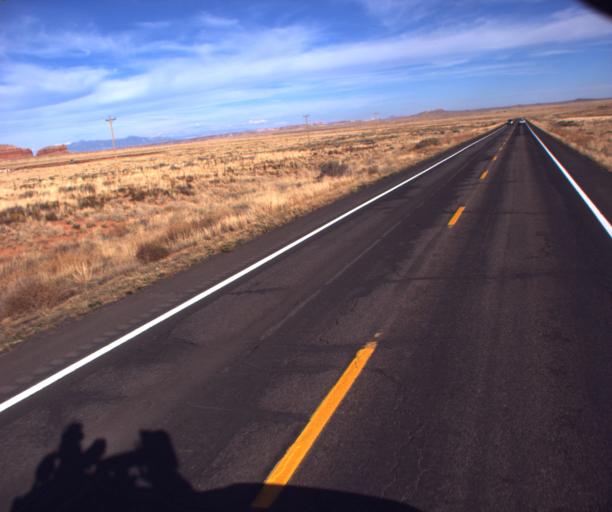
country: US
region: Arizona
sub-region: Apache County
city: Lukachukai
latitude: 36.9587
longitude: -109.3178
